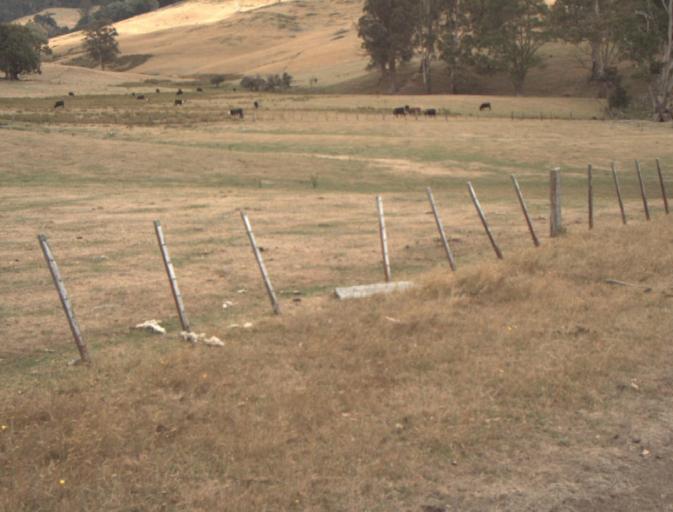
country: AU
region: Tasmania
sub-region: Dorset
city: Scottsdale
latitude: -41.4523
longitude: 147.6012
